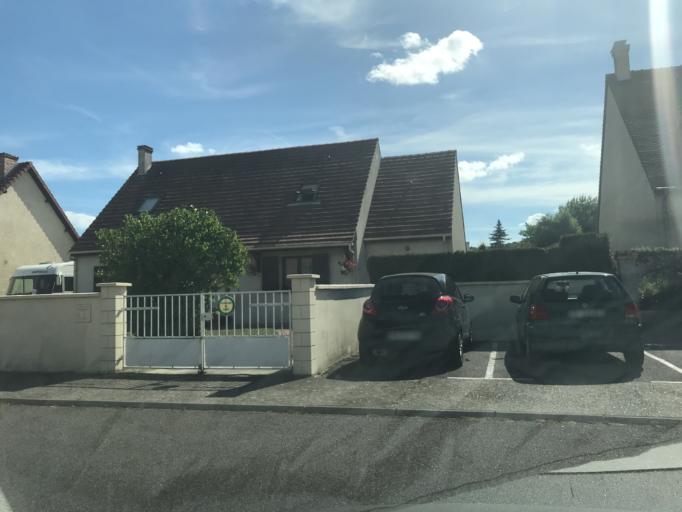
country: FR
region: Haute-Normandie
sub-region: Departement de l'Eure
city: Vernon
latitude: 49.0956
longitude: 1.4577
